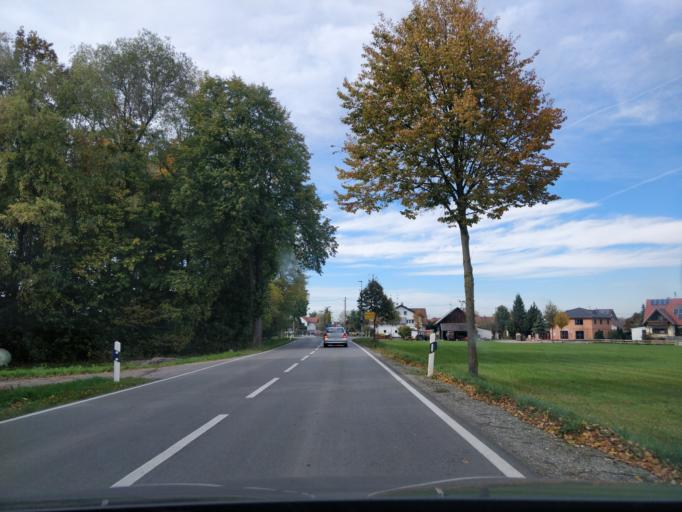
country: DE
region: Bavaria
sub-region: Swabia
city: Wiedergeltingen
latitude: 48.0370
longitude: 10.6813
